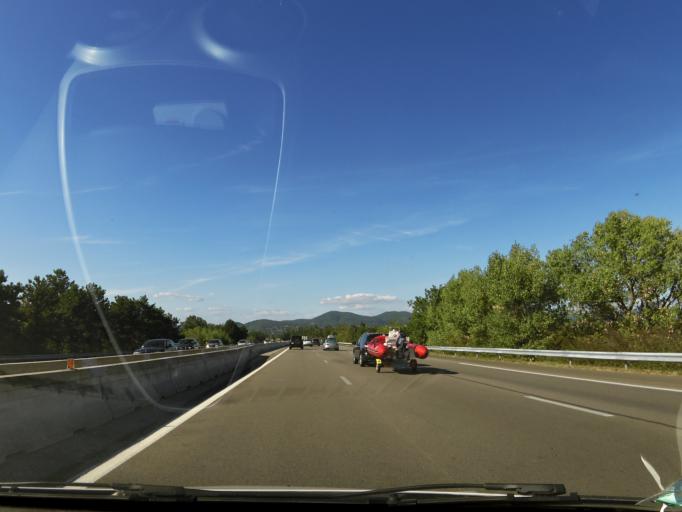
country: FR
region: Rhone-Alpes
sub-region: Departement de la Drome
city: Montboucher-sur-Jabron
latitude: 44.5589
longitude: 4.8113
